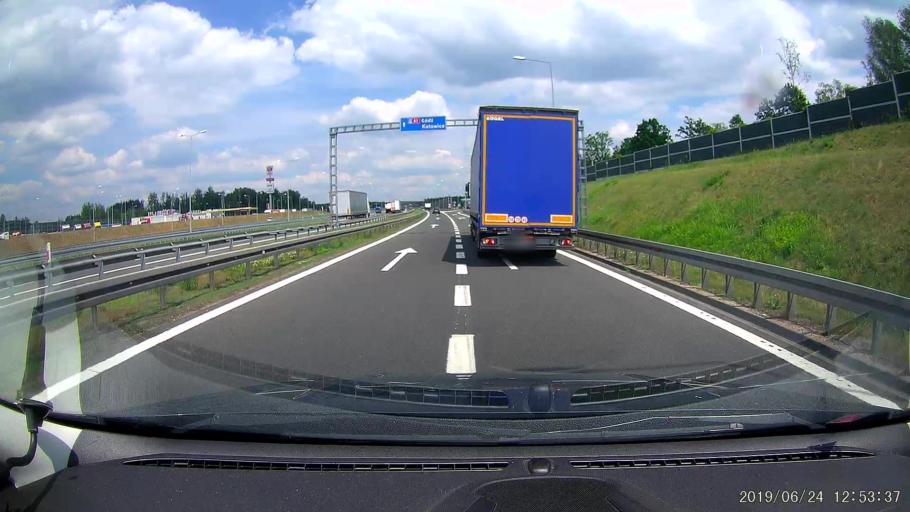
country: PL
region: Silesian Voivodeship
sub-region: Zory
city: Zory
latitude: 50.0725
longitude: 18.6636
